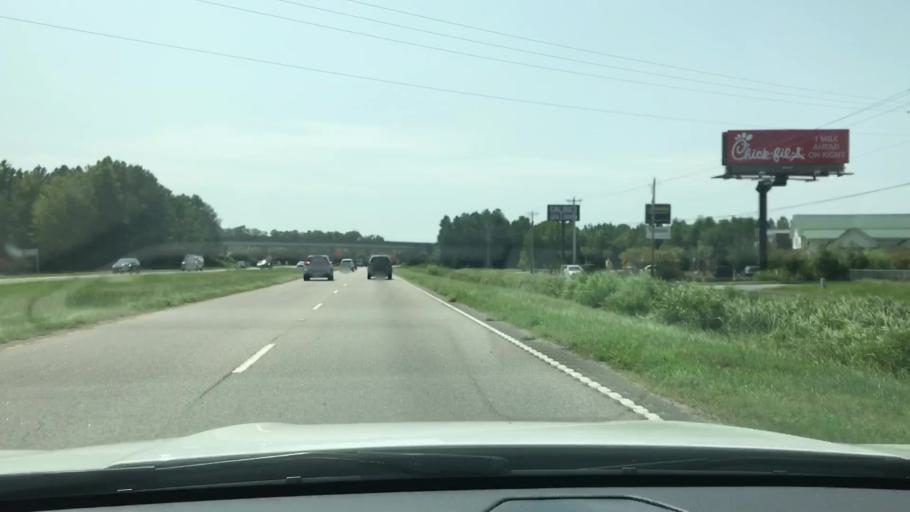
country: US
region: South Carolina
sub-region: Horry County
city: Garden City
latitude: 33.5763
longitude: -79.0292
